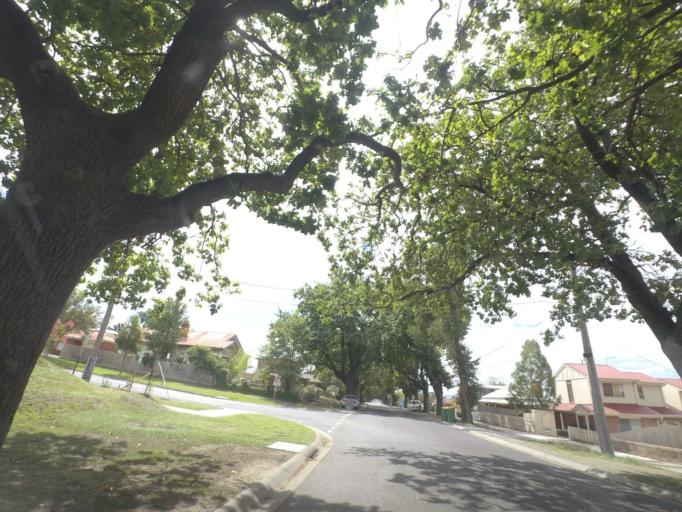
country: AU
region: Victoria
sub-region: Yarra Ranges
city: Lilydale
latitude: -37.7588
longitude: 145.3427
